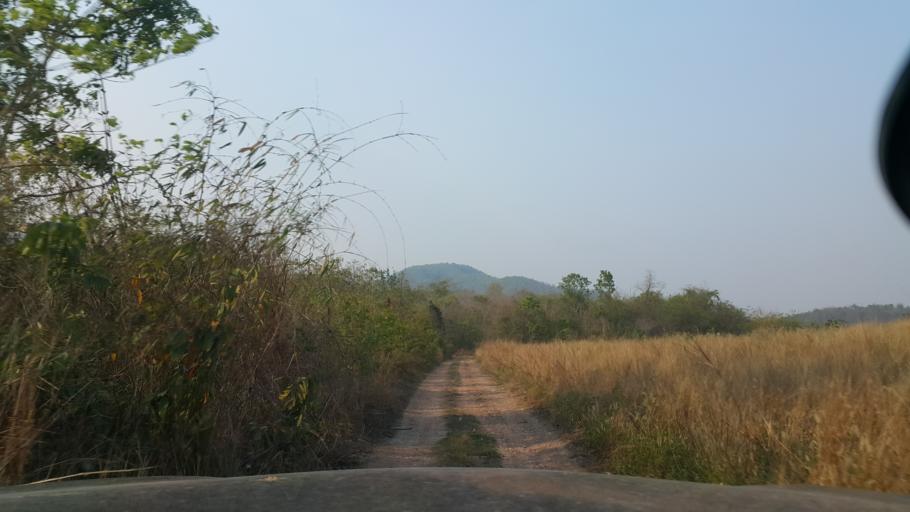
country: TH
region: Sukhothai
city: Thung Saliam
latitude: 17.3359
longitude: 99.4670
